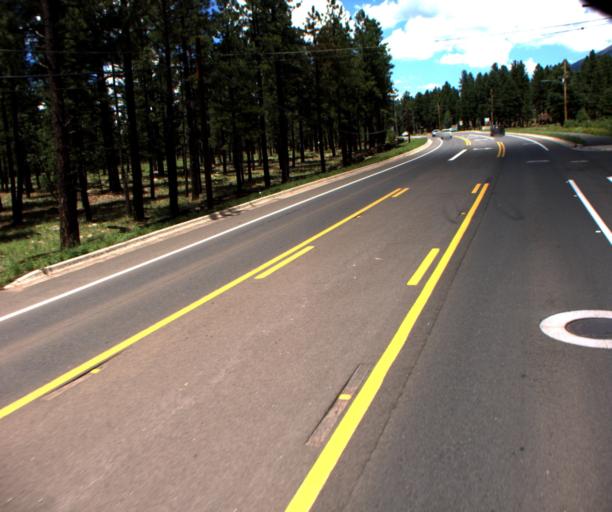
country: US
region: Arizona
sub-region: Coconino County
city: Flagstaff
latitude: 35.2308
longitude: -111.6608
